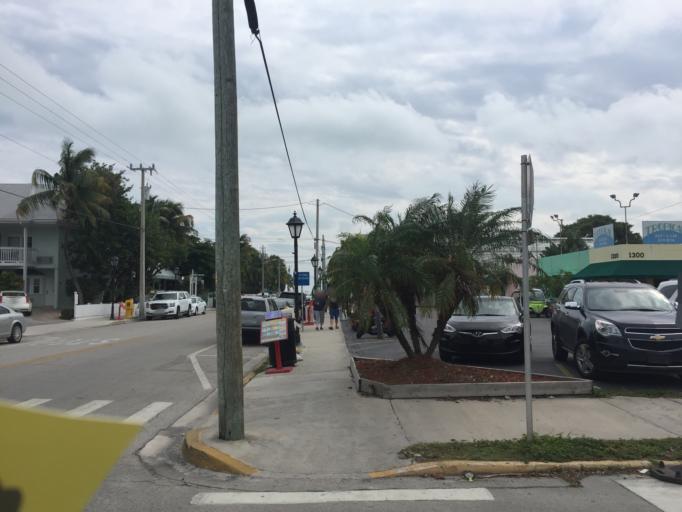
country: US
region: Florida
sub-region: Monroe County
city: Key West
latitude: 24.5483
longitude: -81.7973
